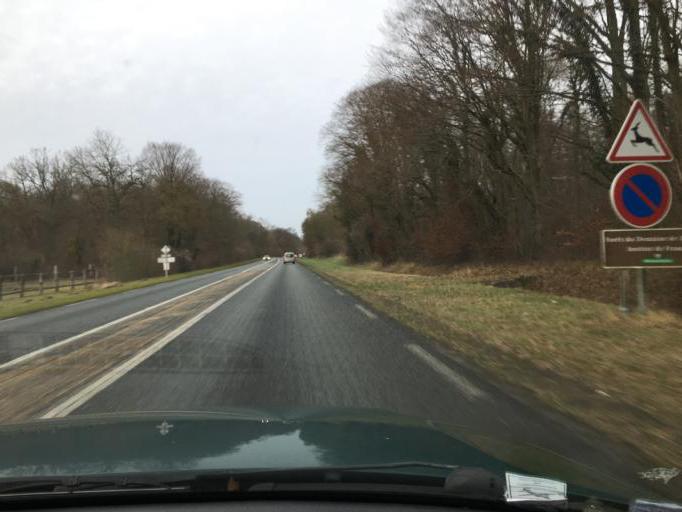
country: FR
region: Picardie
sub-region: Departement de l'Oise
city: Thiers-sur-Theve
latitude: 49.1580
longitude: 2.5517
